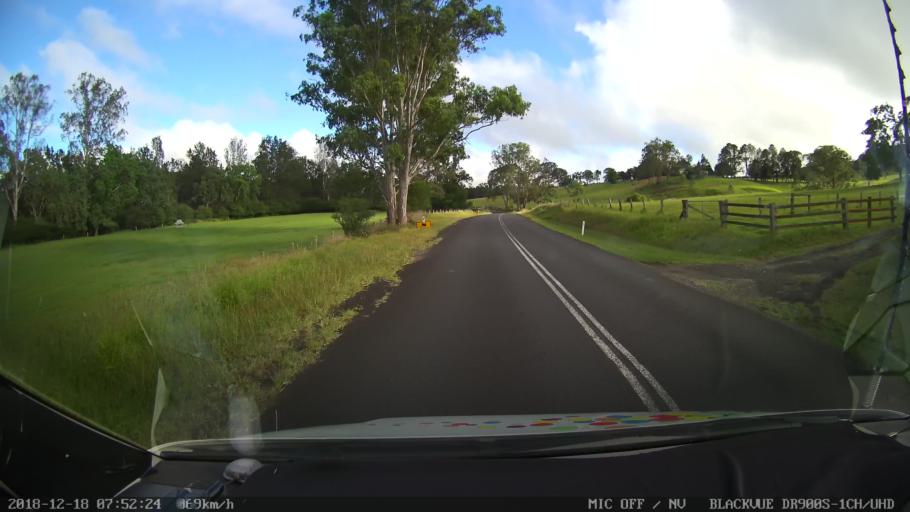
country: AU
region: New South Wales
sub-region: Kyogle
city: Kyogle
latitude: -28.4289
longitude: 152.5809
